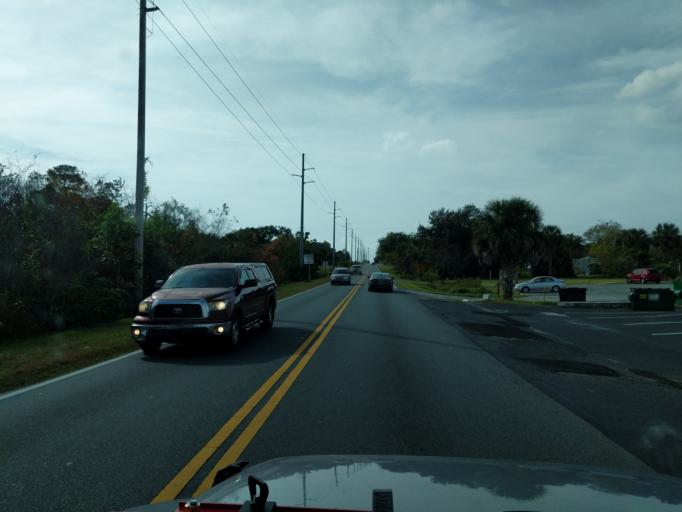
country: US
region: Florida
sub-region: Lake County
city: Mount Dora
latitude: 28.8073
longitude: -81.6760
